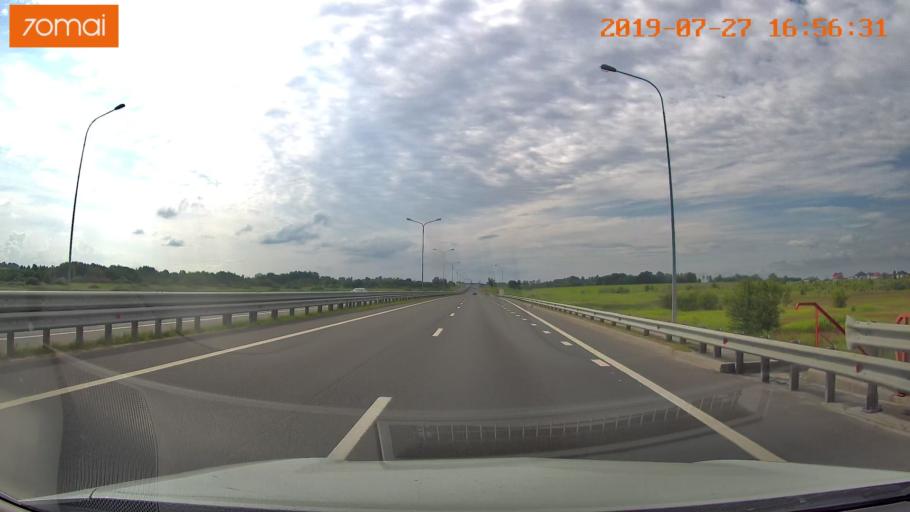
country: RU
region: Kaliningrad
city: Bol'shoe Isakovo
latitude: 54.6950
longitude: 20.7372
